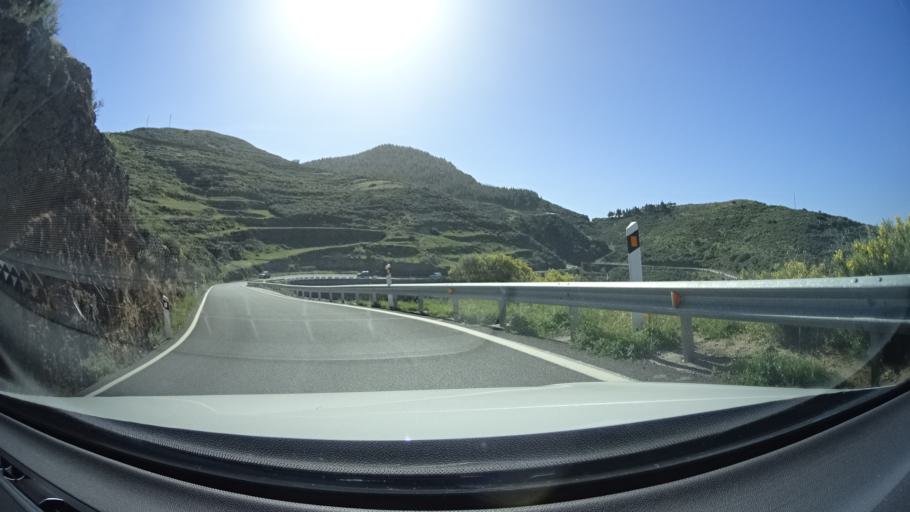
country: ES
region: Canary Islands
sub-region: Provincia de Las Palmas
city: Artenara
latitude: 28.0241
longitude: -15.6440
